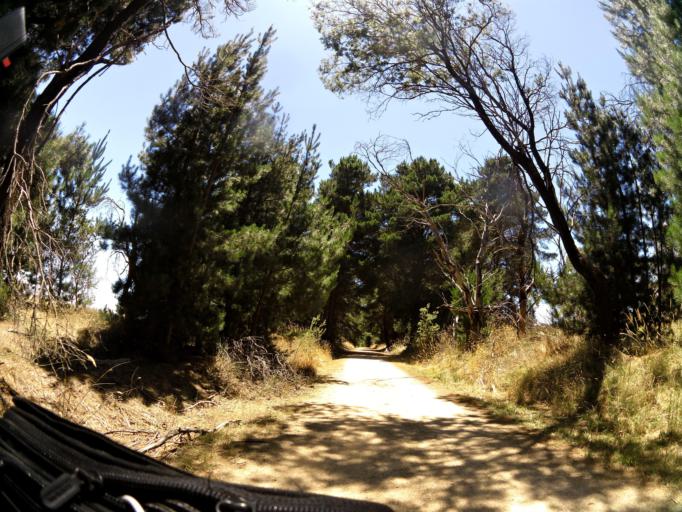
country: AU
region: Victoria
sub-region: Ballarat North
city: Delacombe
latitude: -37.5844
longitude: 143.7245
